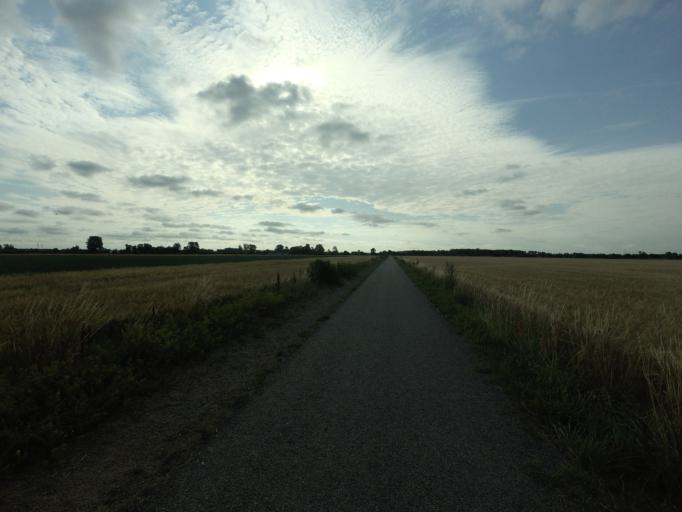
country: SE
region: Skane
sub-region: Hoganas Kommun
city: Hoganas
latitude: 56.1848
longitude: 12.6418
